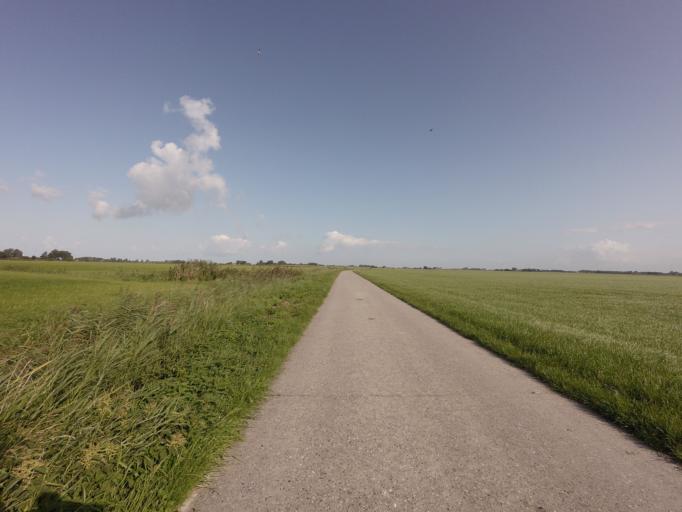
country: NL
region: Friesland
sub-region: Gemeente Franekeradeel
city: Franeker
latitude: 53.2021
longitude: 5.5772
